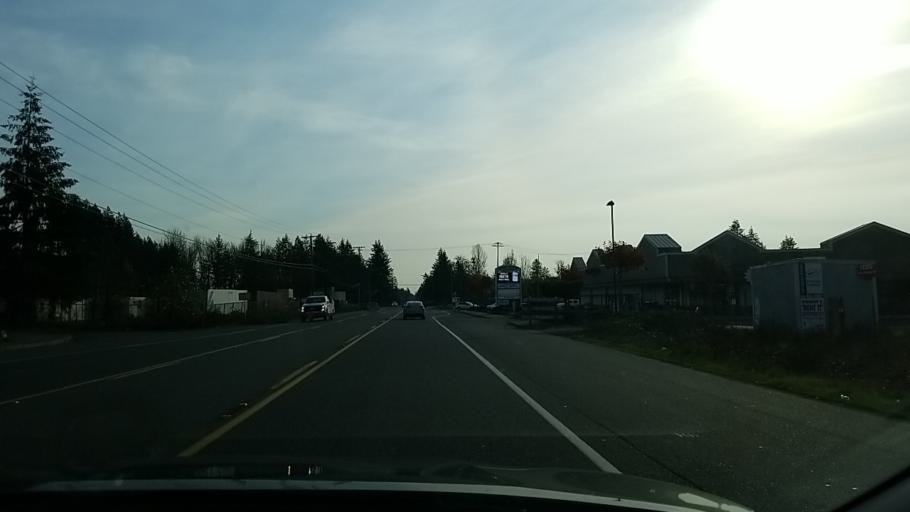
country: US
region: Washington
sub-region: Thurston County
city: Grand Mound
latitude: 46.7991
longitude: -123.0122
